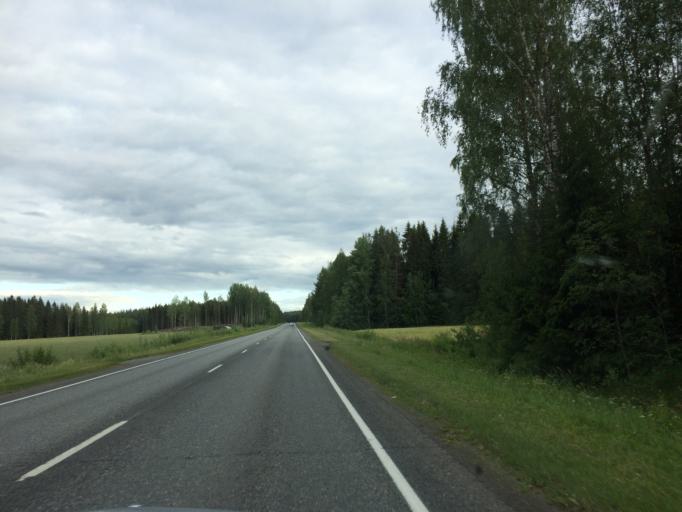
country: FI
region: Haeme
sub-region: Haemeenlinna
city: Janakkala
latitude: 60.9336
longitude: 24.5267
